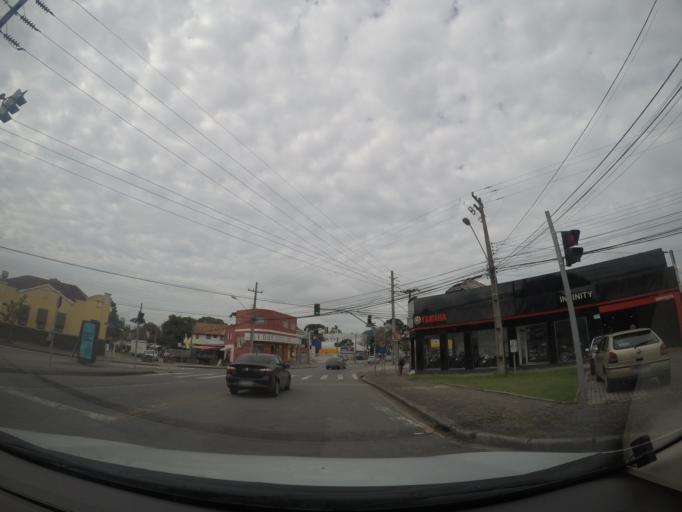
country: BR
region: Parana
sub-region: Curitiba
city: Curitiba
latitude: -25.4128
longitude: -49.2798
